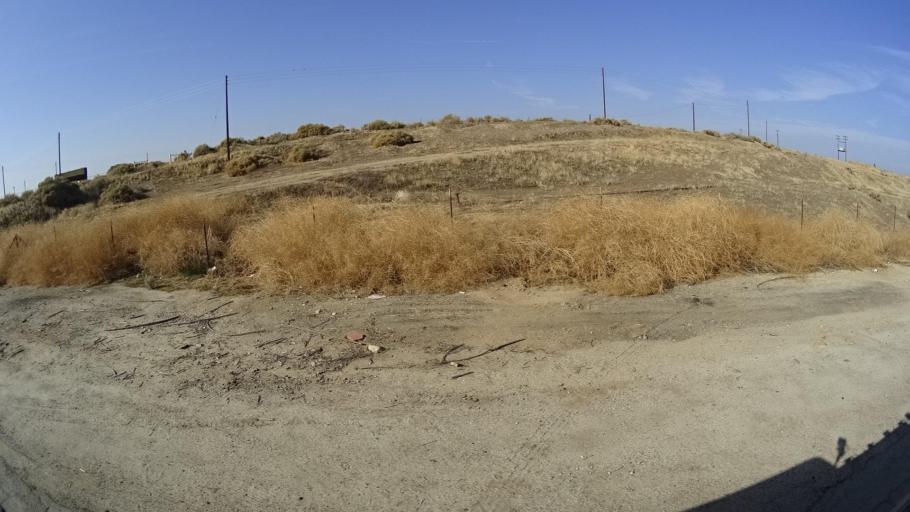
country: US
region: California
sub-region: Kern County
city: Oildale
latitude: 35.4627
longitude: -119.0494
